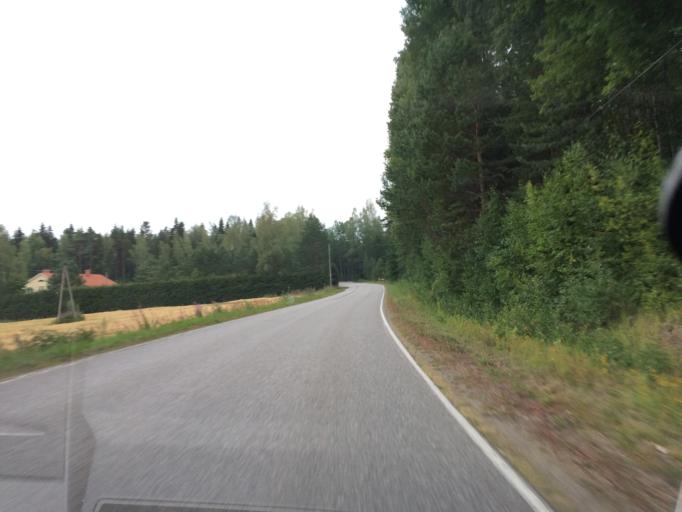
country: FI
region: Haeme
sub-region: Haemeenlinna
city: Tuulos
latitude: 61.2149
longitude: 24.7311
